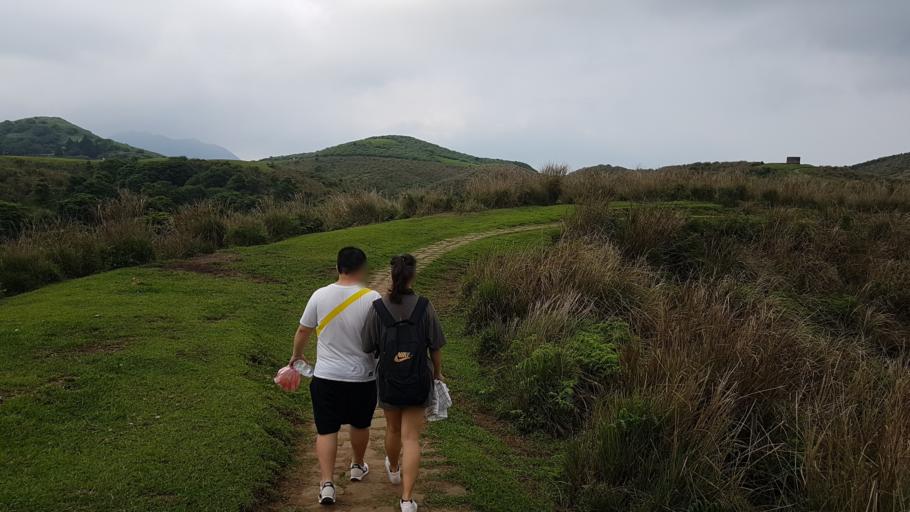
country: TW
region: Taipei
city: Taipei
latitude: 25.1623
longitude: 121.5764
